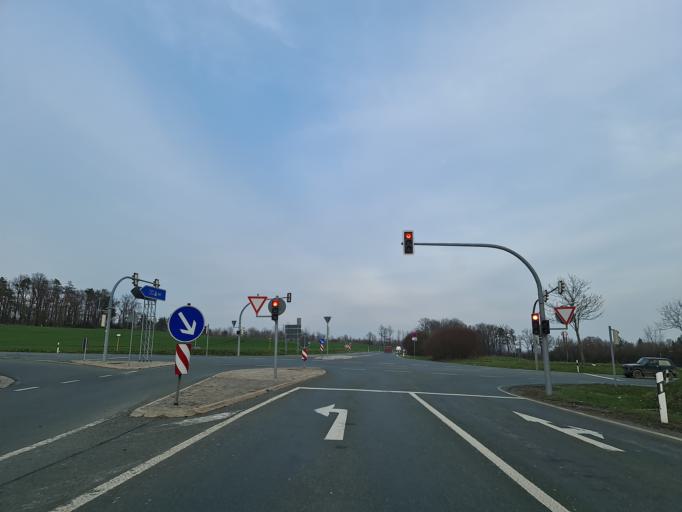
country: DE
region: Saxony
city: Weischlitz
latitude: 50.4367
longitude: 12.0912
